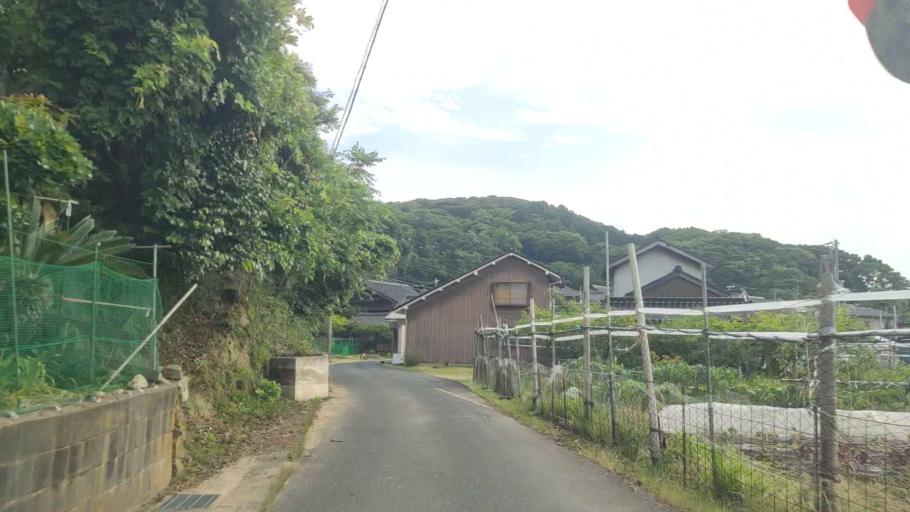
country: JP
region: Hyogo
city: Toyooka
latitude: 35.6433
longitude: 134.8988
